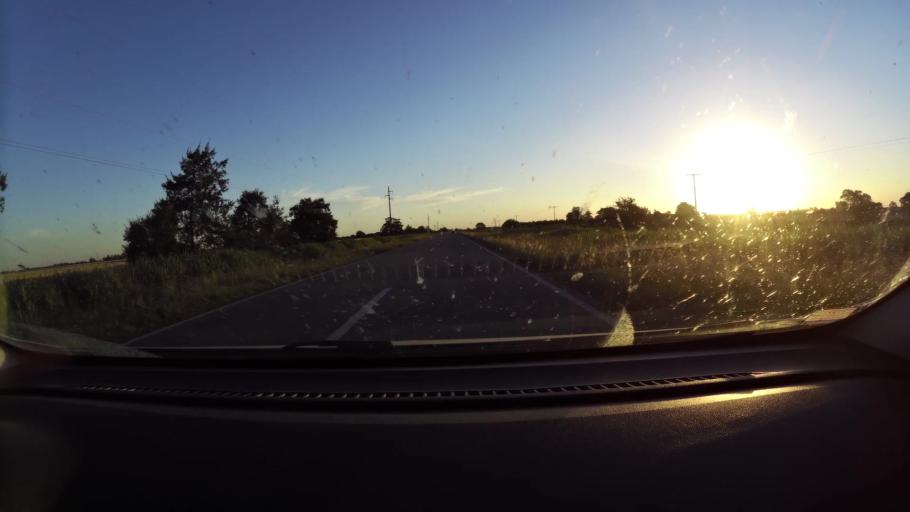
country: AR
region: Cordoba
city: Villa Maria
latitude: -32.2737
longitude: -63.2179
